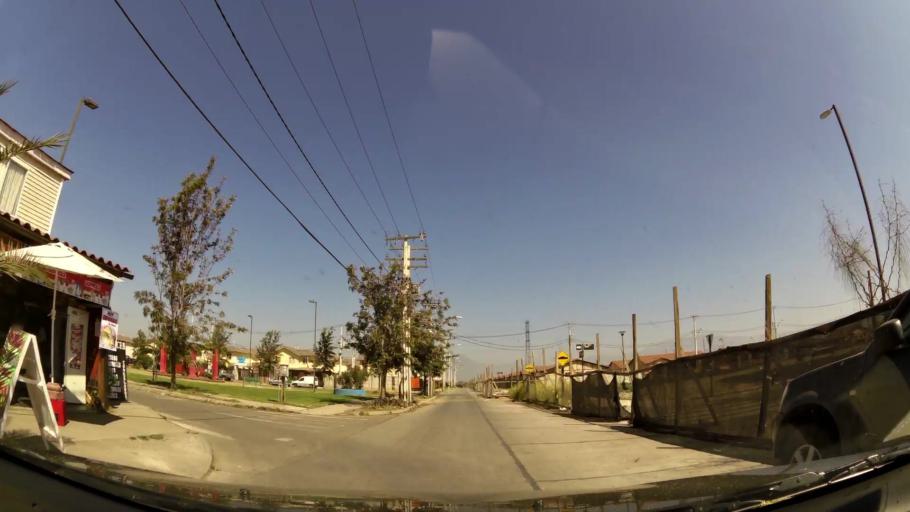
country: CL
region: Santiago Metropolitan
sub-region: Provincia de Chacabuco
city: Chicureo Abajo
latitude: -33.3294
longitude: -70.7505
